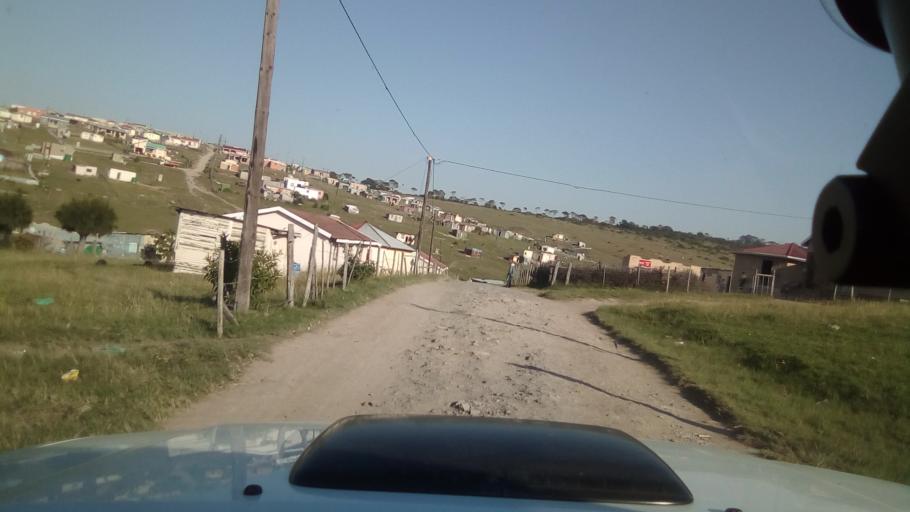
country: ZA
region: Eastern Cape
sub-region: Buffalo City Metropolitan Municipality
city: East London
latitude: -32.8483
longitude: 27.9886
